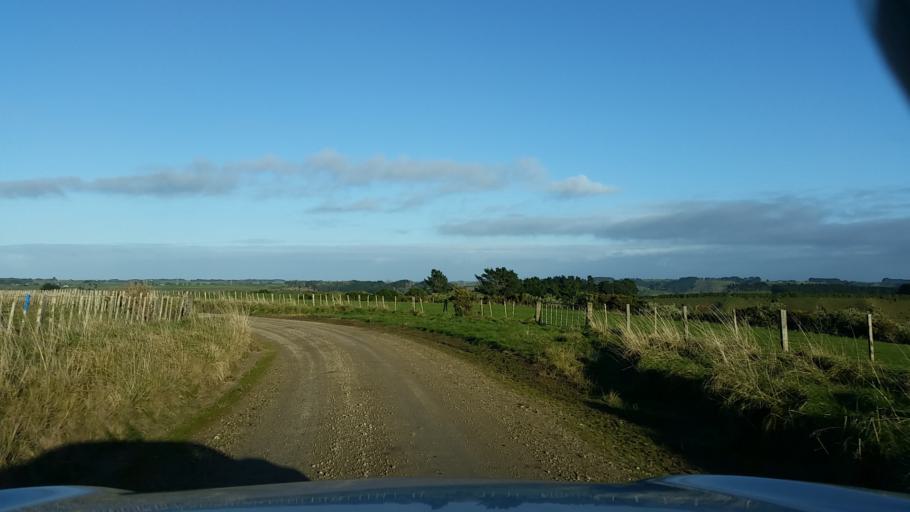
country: NZ
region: Taranaki
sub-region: South Taranaki District
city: Patea
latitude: -39.7560
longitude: 174.7439
